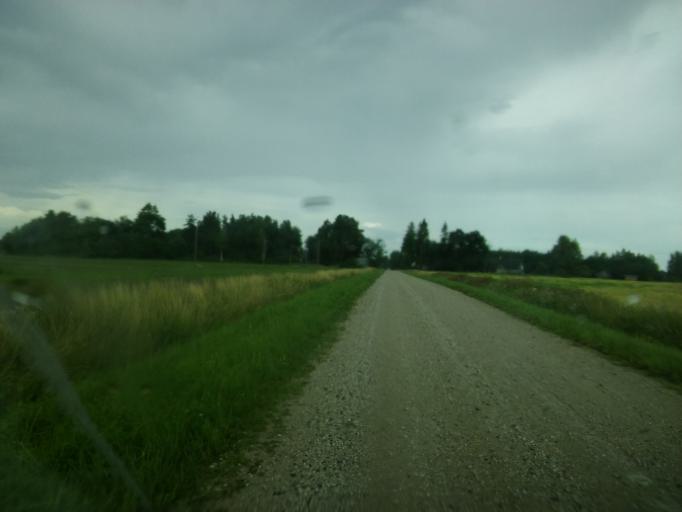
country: EE
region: Paernumaa
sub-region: Halinga vald
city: Parnu-Jaagupi
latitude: 58.7839
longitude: 24.5763
